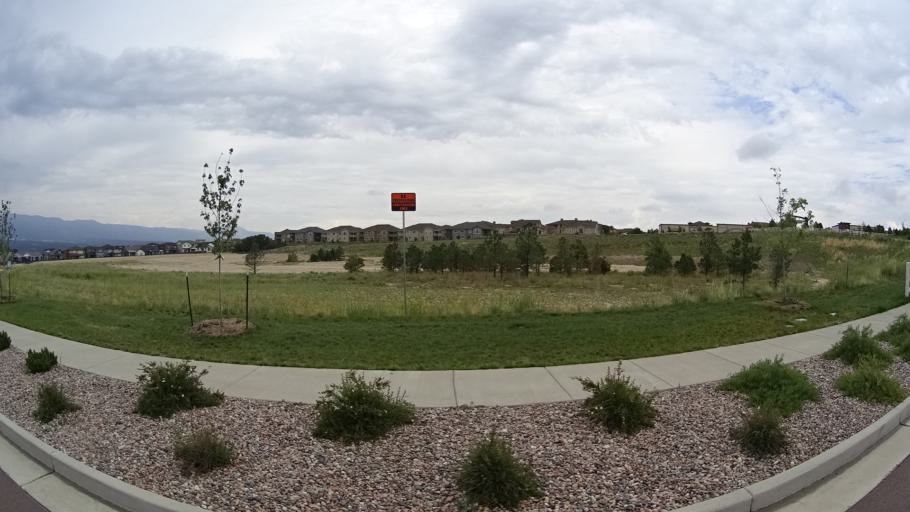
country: US
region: Colorado
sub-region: El Paso County
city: Gleneagle
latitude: 39.0006
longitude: -104.8005
